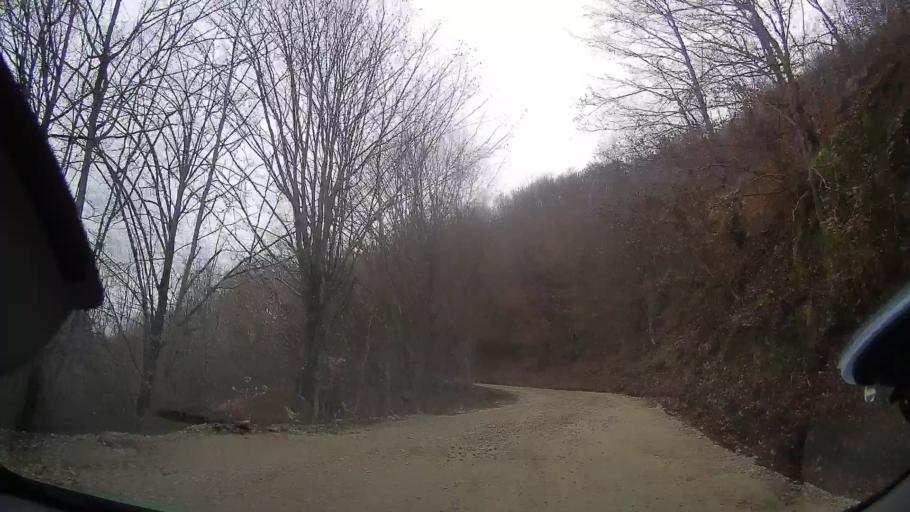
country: RO
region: Cluj
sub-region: Comuna Maguri-Racatau
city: Maguri-Racatau
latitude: 46.6515
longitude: 23.1942
